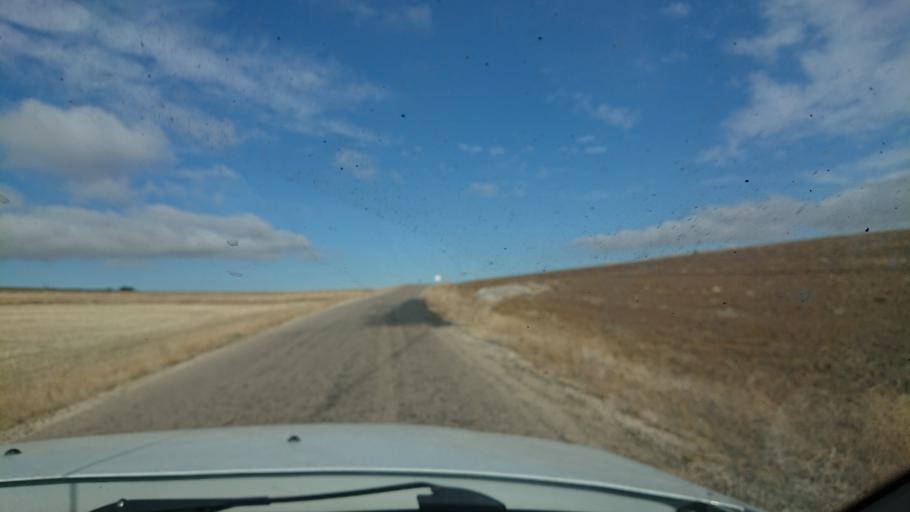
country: TR
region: Aksaray
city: Agacoren
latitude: 38.8363
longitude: 33.9543
